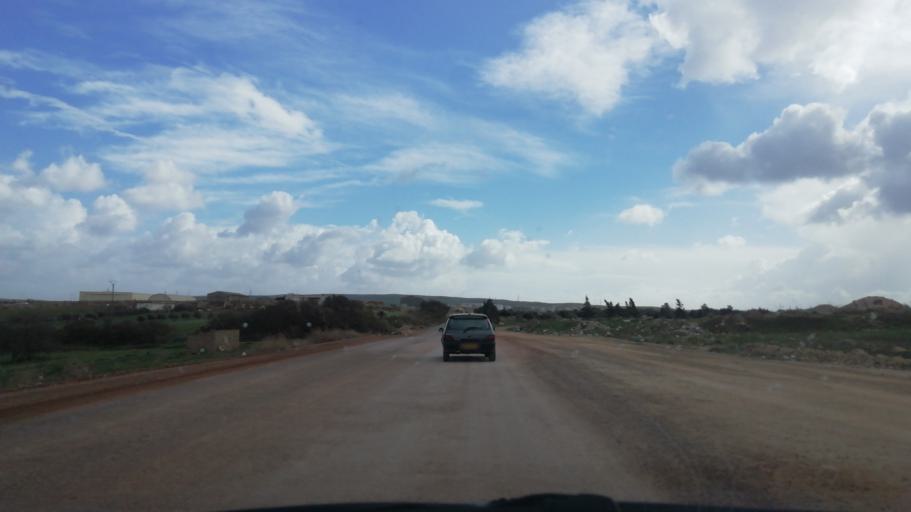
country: DZ
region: Oran
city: Sidi ech Chahmi
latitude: 35.6350
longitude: -0.5365
